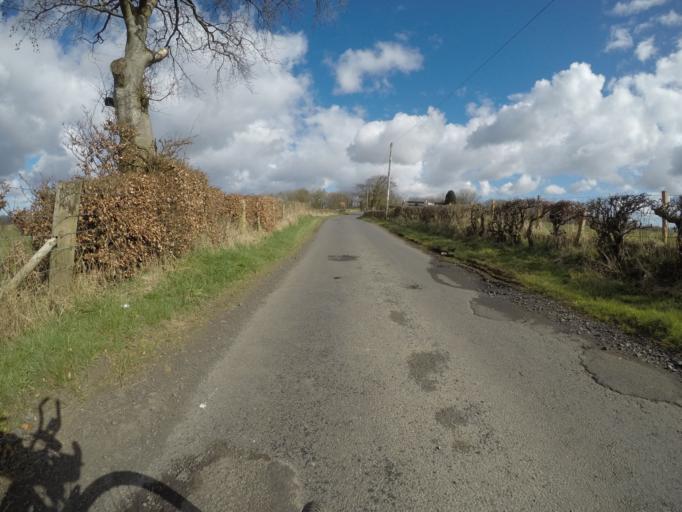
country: GB
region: Scotland
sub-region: North Ayrshire
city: Beith
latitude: 55.7177
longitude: -4.6200
